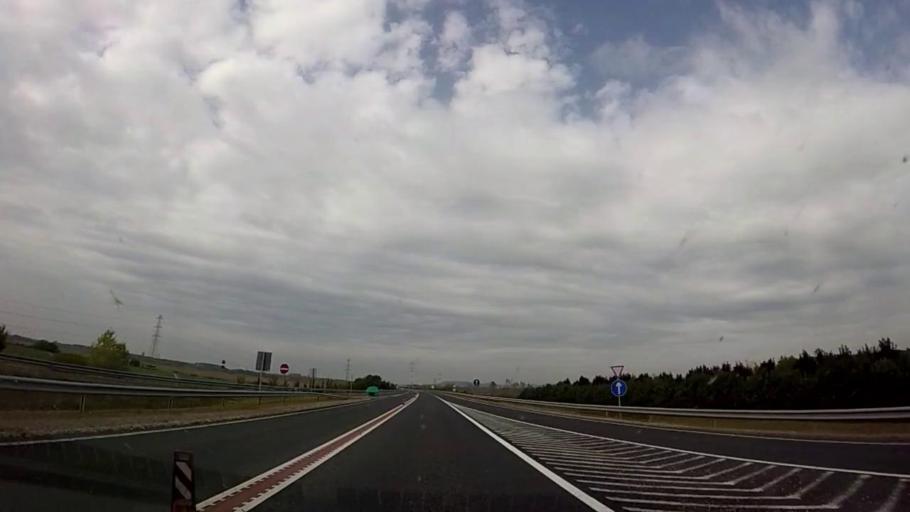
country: HR
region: Medimurska
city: Domasinec
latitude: 46.5031
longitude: 16.6077
